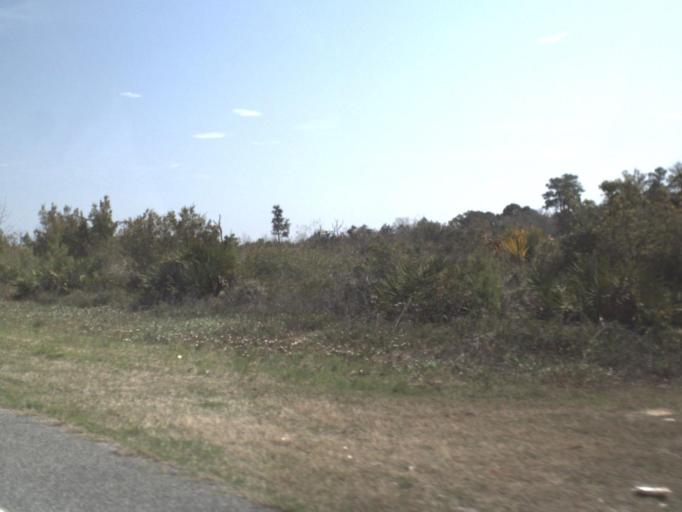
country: US
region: Florida
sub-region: Franklin County
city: Apalachicola
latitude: 29.7222
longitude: -85.0724
